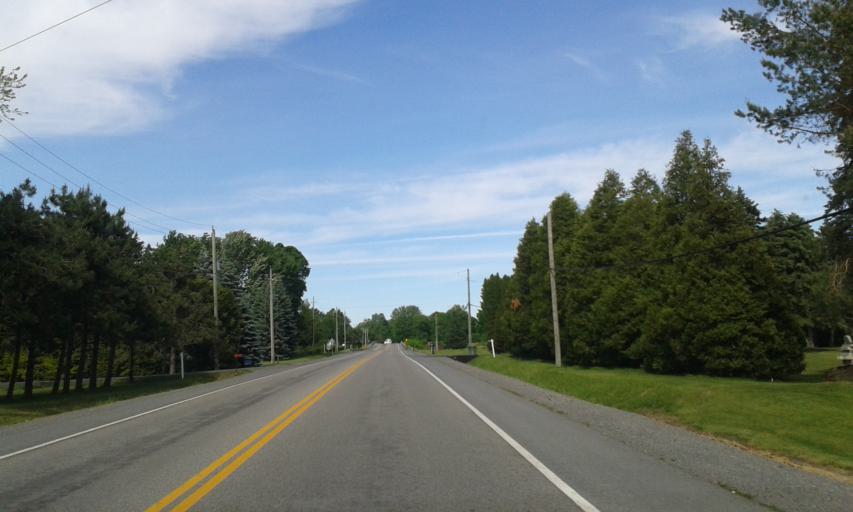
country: CA
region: Ontario
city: Cornwall
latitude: 45.1265
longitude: -74.4980
